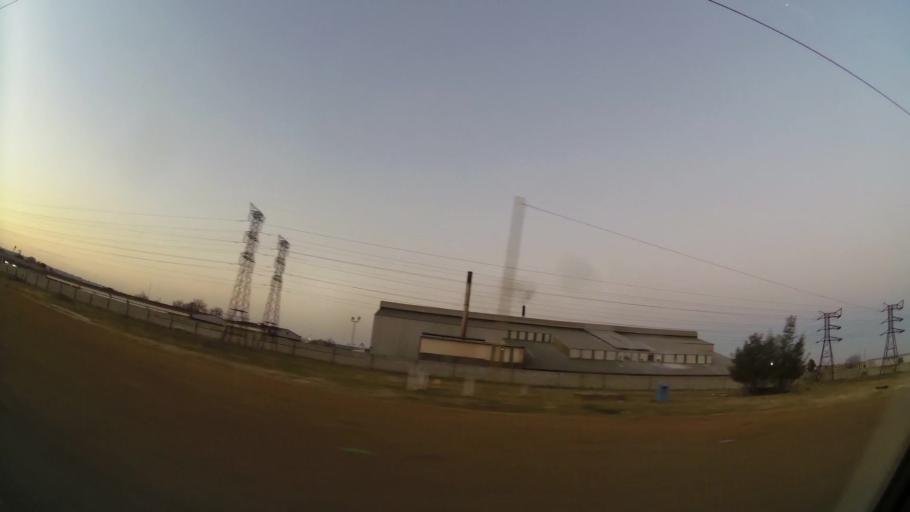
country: ZA
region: Gauteng
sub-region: Ekurhuleni Metropolitan Municipality
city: Germiston
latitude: -26.2780
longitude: 28.1709
